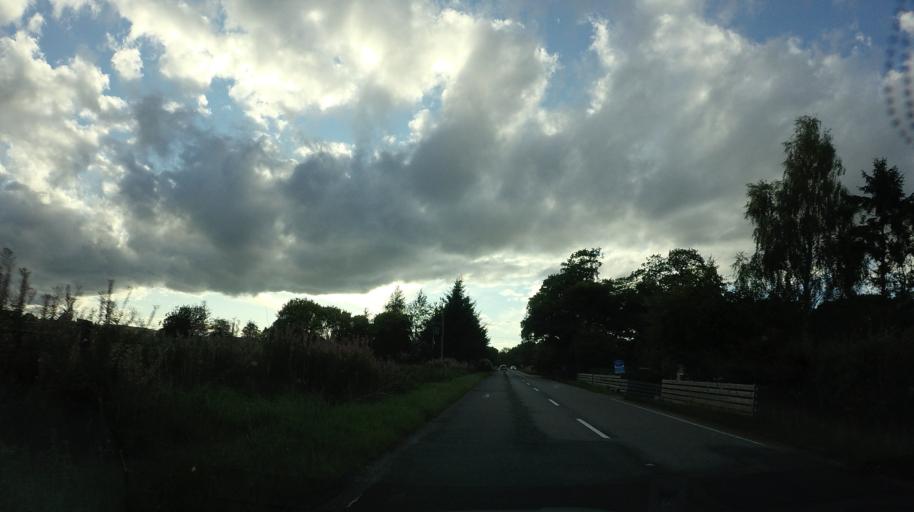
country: GB
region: Scotland
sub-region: Aberdeenshire
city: Alford
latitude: 57.2319
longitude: -2.6691
